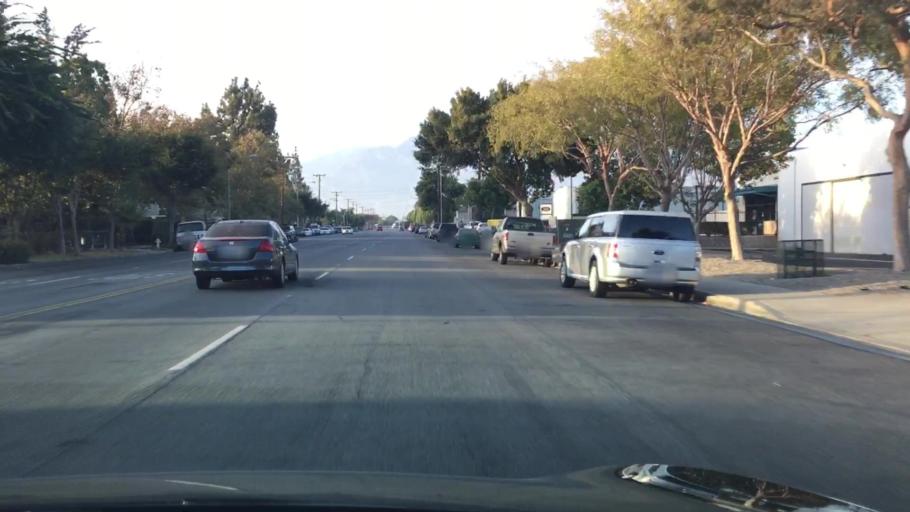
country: US
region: California
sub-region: San Bernardino County
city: Ontario
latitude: 34.0424
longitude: -117.6416
